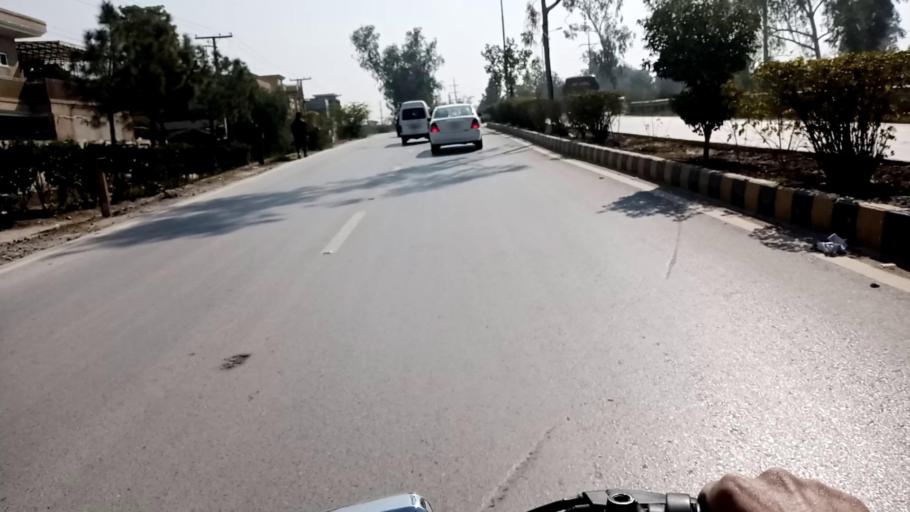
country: PK
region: Khyber Pakhtunkhwa
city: Peshawar
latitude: 33.9626
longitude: 71.4324
